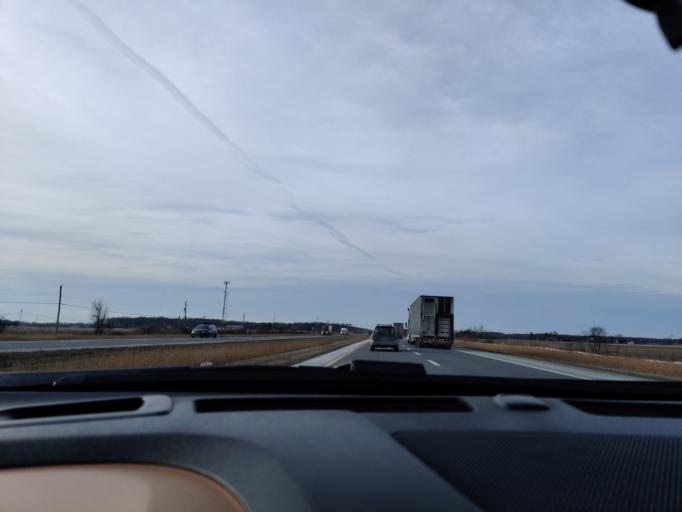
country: CA
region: Quebec
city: Les Cedres
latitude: 45.3304
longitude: -74.1125
